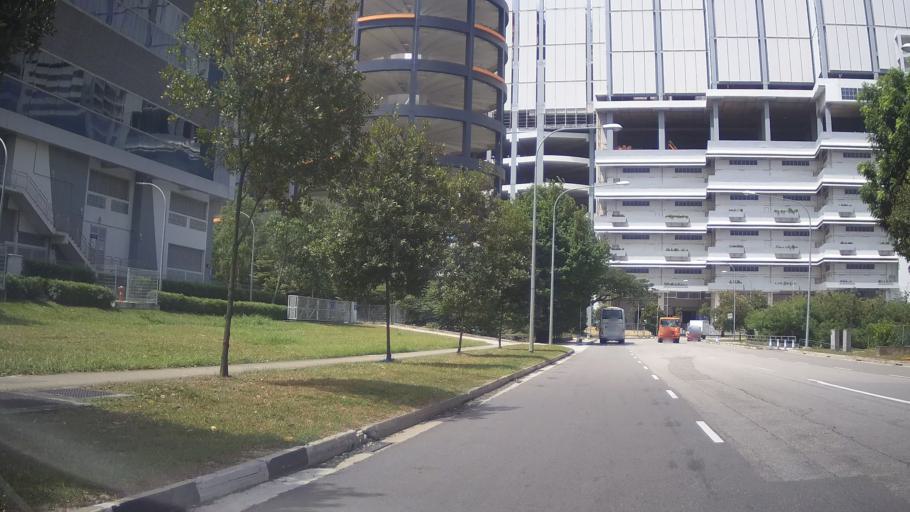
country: SG
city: Singapore
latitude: 1.3121
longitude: 103.6997
